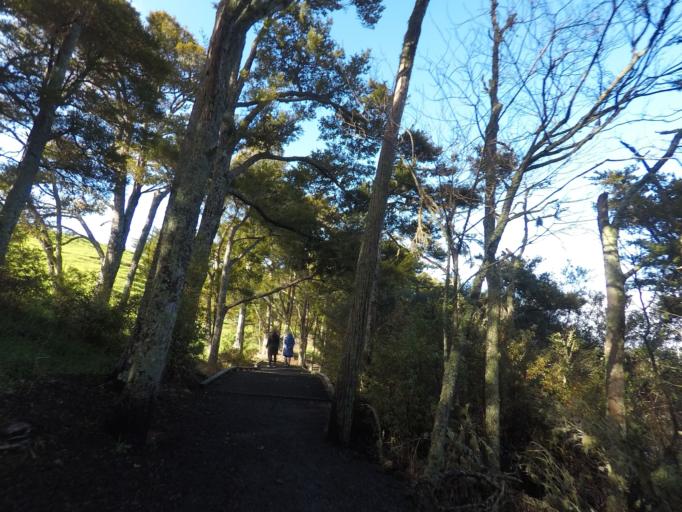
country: NZ
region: Auckland
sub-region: Auckland
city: Warkworth
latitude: -36.4287
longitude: 174.7184
